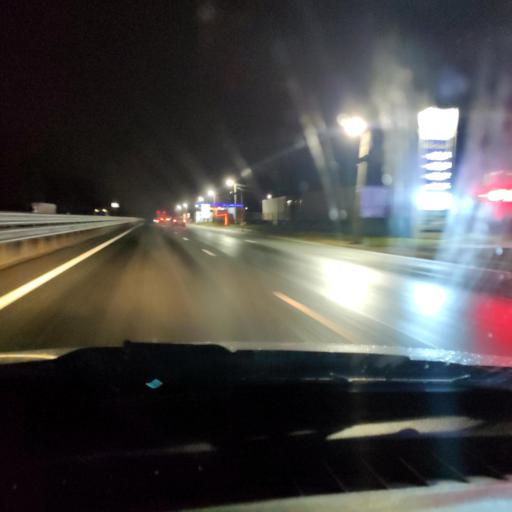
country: RU
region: Samara
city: Zhigulevsk
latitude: 53.5032
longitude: 49.5485
